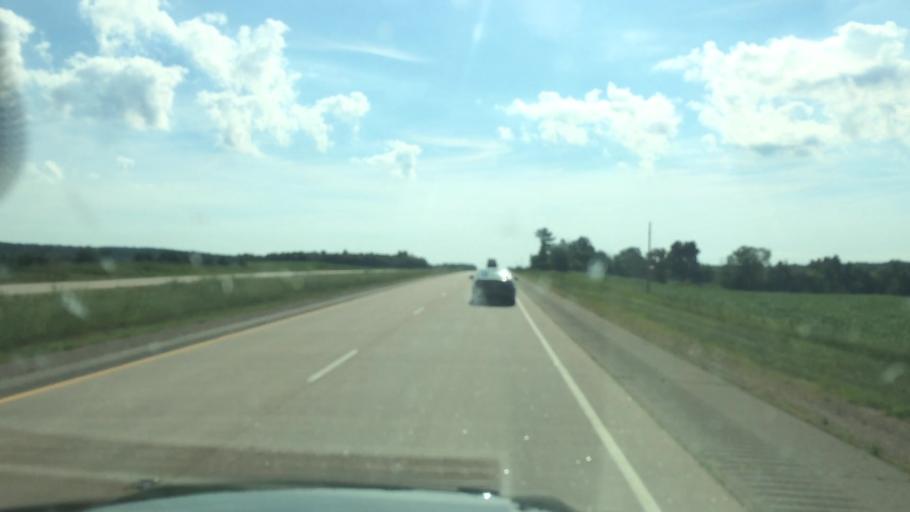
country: US
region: Wisconsin
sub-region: Shawano County
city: Wittenberg
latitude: 44.8039
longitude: -89.0045
